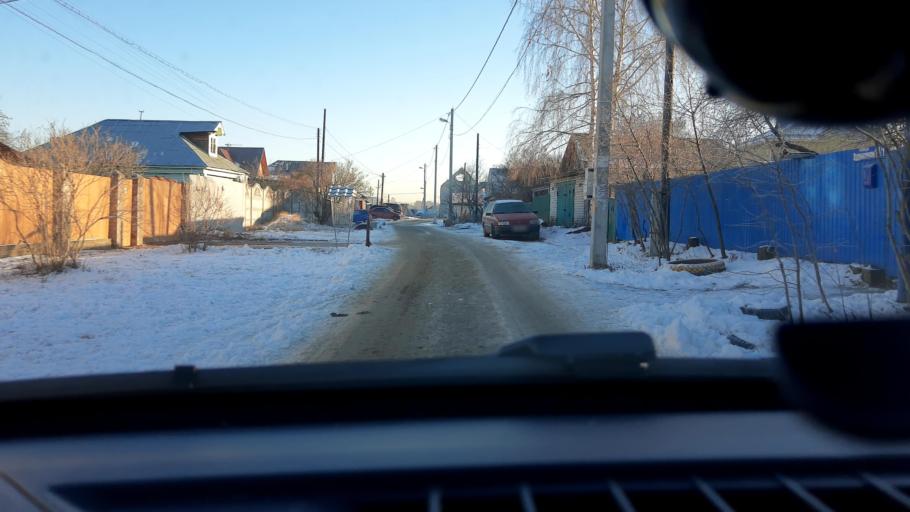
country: RU
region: Nizjnij Novgorod
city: Gorbatovka
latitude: 56.3328
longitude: 43.8234
